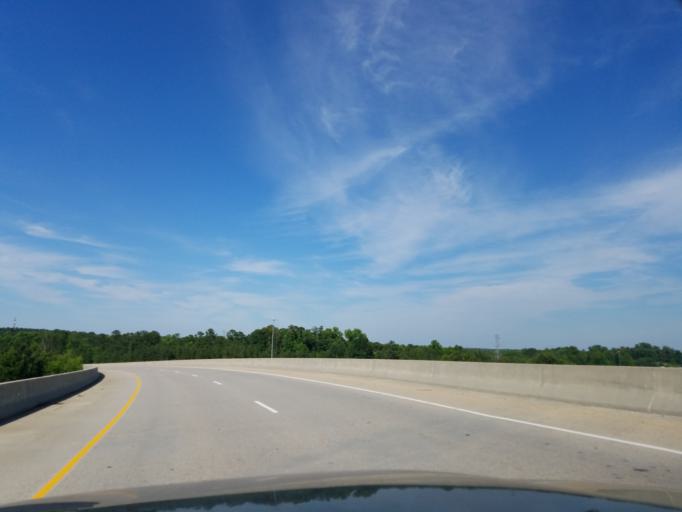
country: US
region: North Carolina
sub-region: Wake County
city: Raleigh
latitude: 35.8746
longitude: -78.5750
